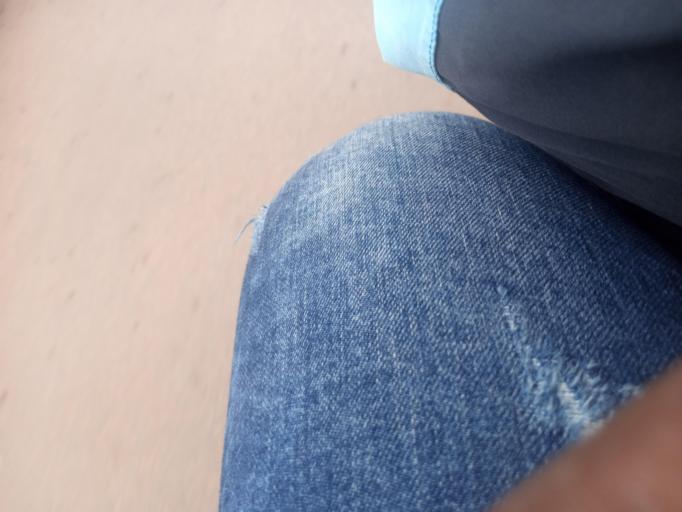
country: SL
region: Southern Province
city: Bo
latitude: 7.9663
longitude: -11.7368
